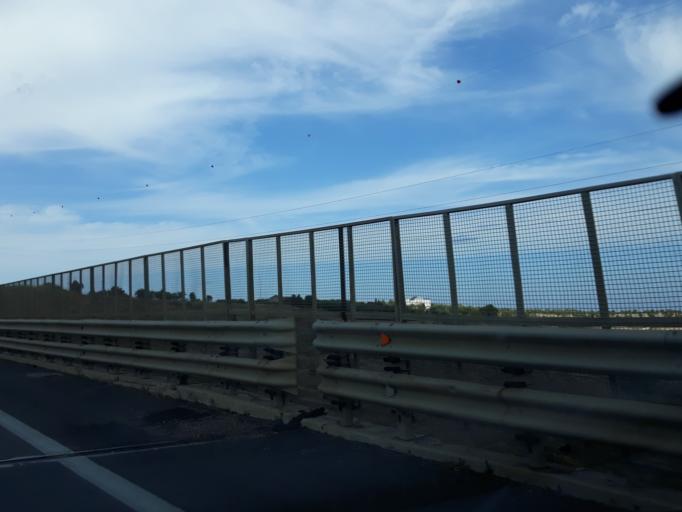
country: IT
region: Sicily
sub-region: Palermo
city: Termini Imerese
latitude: 37.9796
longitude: 13.6724
